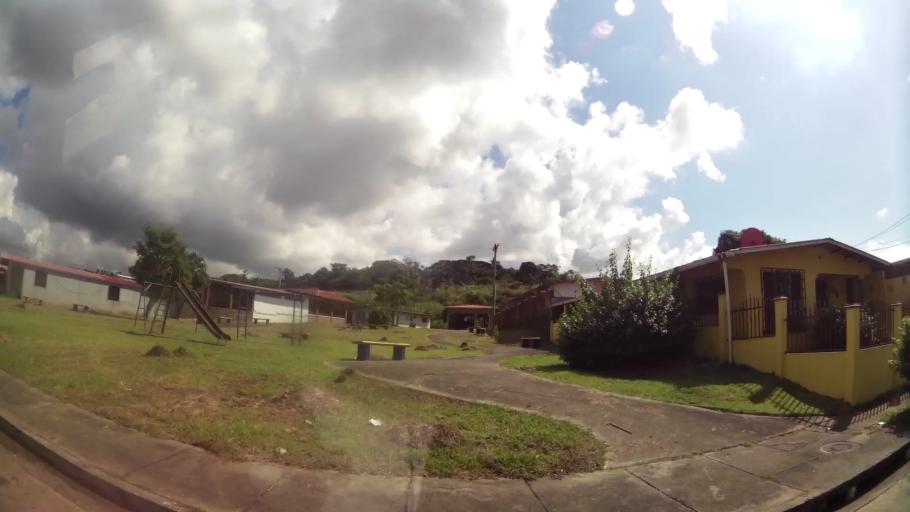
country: PA
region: Panama
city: Nuevo Arraijan
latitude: 8.9123
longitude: -79.7409
